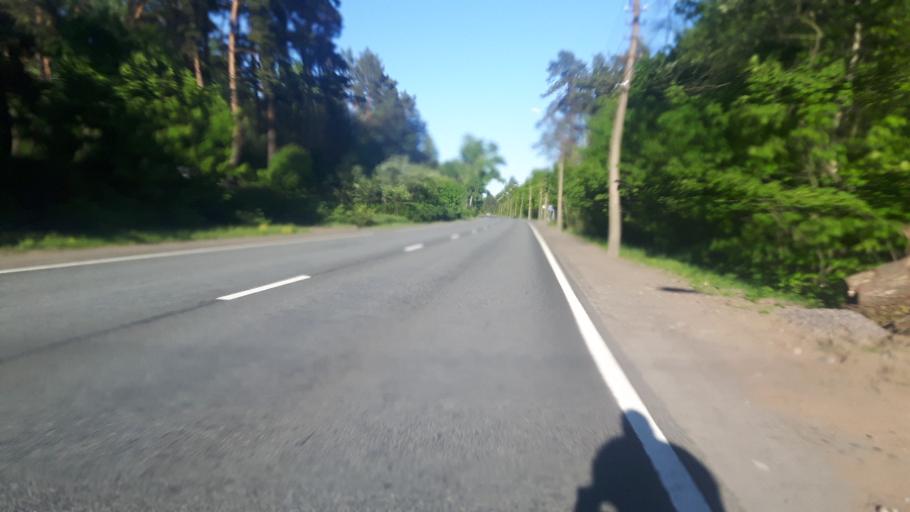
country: RU
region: Leningrad
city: Molodezhnoye
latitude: 60.1799
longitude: 29.4665
